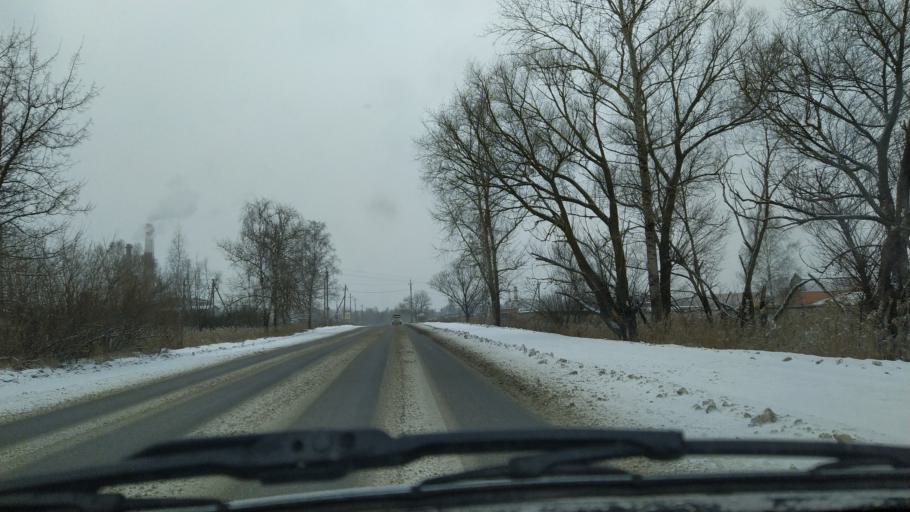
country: RU
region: Moskovskaya
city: Lopatinskiy
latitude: 55.3469
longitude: 38.7363
